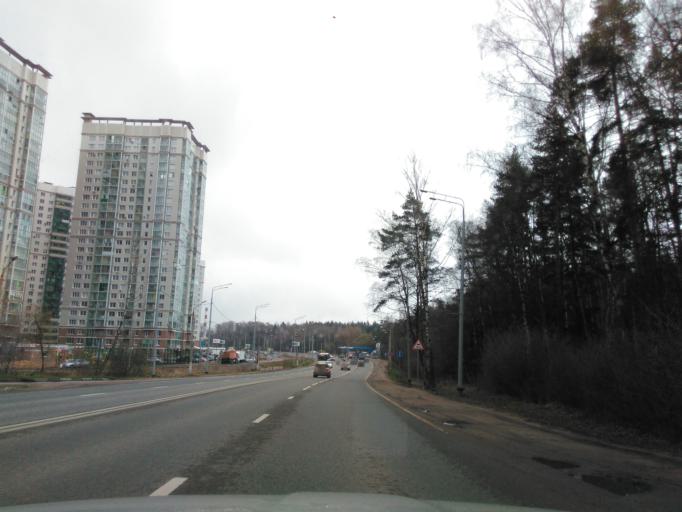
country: RU
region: Moskovskaya
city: Opalikha
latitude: 55.8348
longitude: 37.2660
